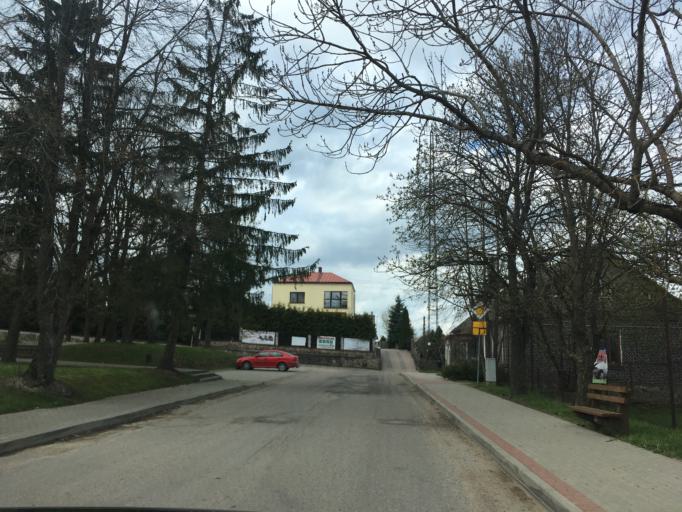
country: PL
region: Podlasie
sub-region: Suwalki
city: Suwalki
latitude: 54.3676
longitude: 22.8694
